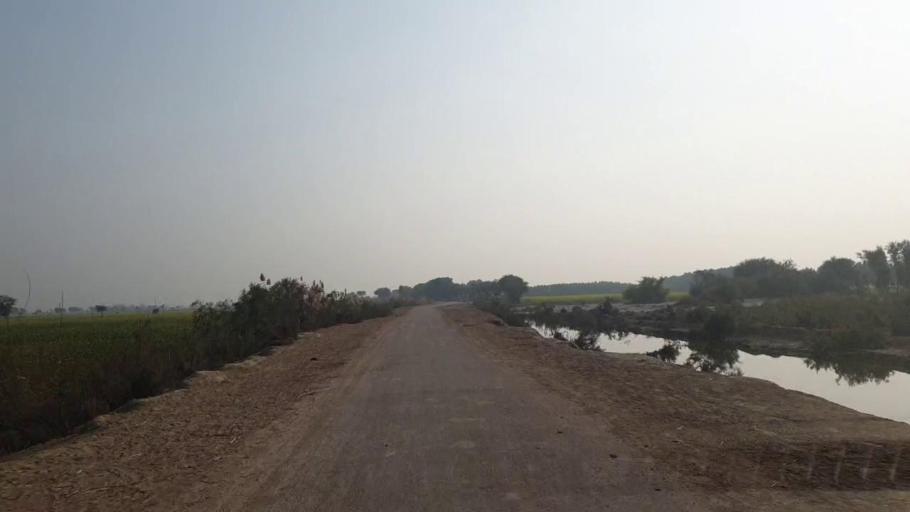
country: PK
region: Sindh
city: Shahdadpur
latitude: 25.9668
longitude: 68.5233
